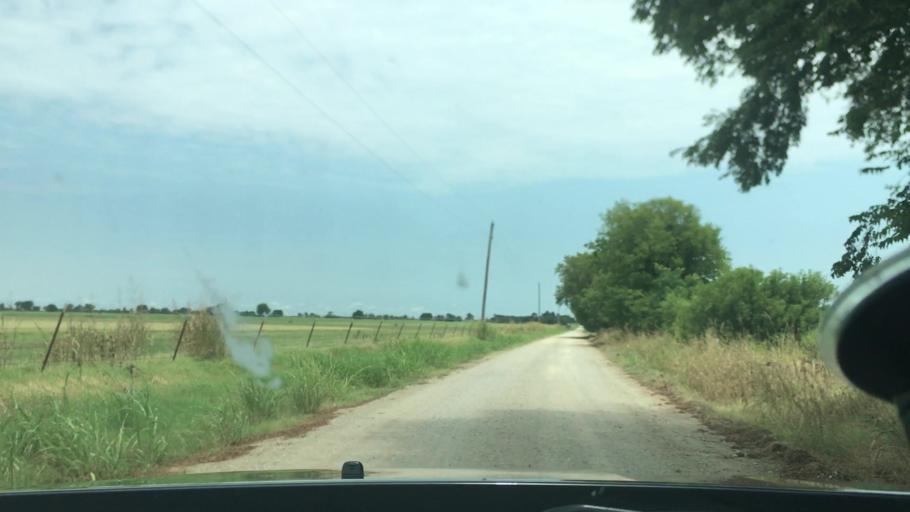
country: US
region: Texas
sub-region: Cooke County
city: Muenster
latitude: 33.8606
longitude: -97.3870
